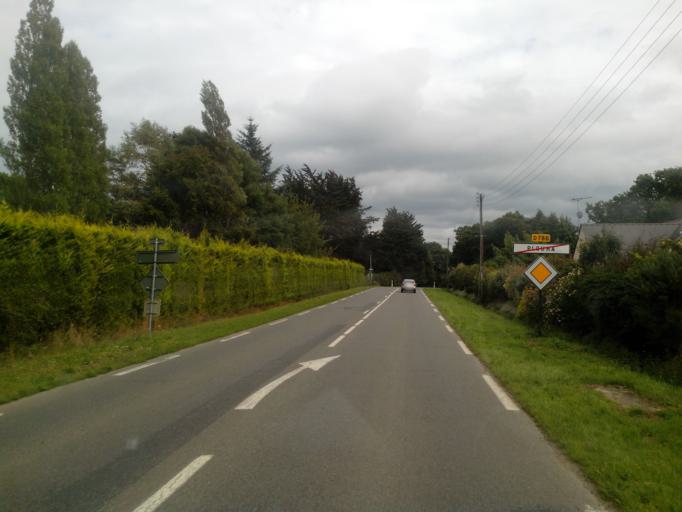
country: FR
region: Brittany
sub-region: Departement des Cotes-d'Armor
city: Plouha
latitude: 48.6680
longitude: -2.9146
